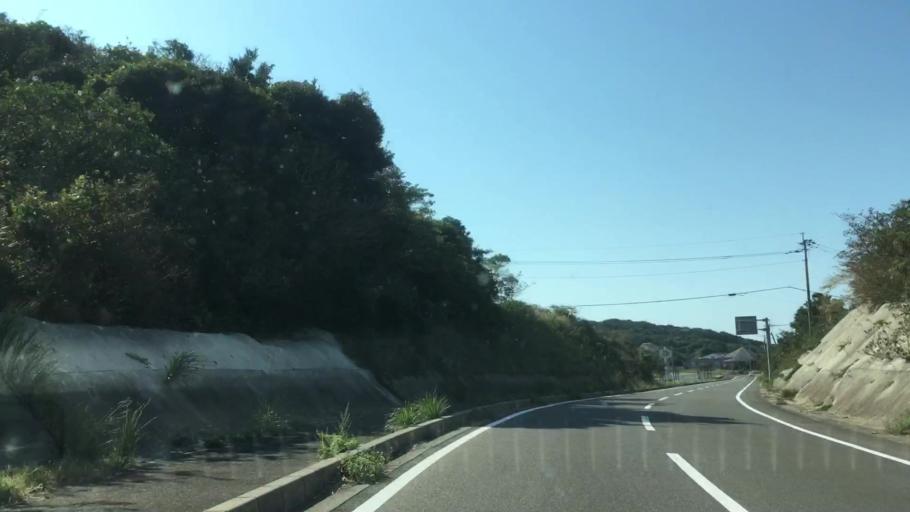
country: JP
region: Nagasaki
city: Sasebo
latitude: 33.0187
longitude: 129.5744
